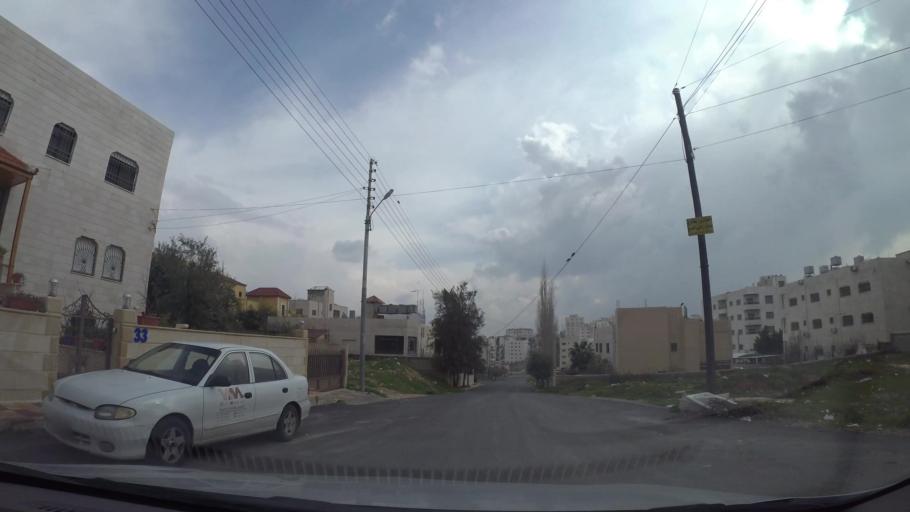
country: JO
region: Amman
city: Umm as Summaq
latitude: 31.8860
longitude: 35.8645
